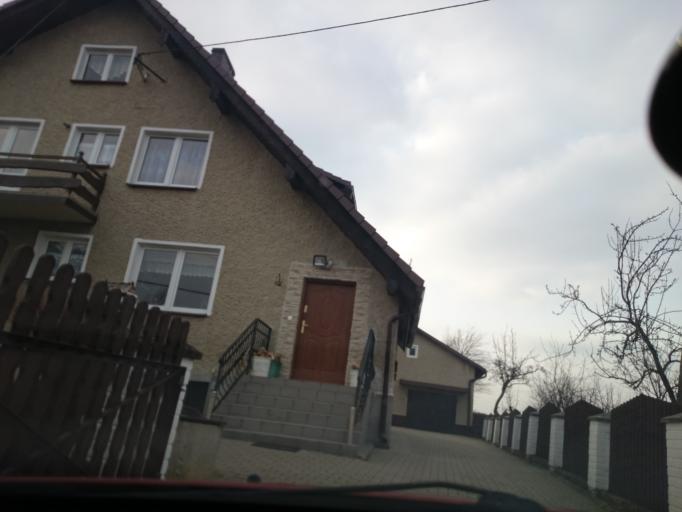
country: PL
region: Lower Silesian Voivodeship
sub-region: Powiat zabkowicki
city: Bardo
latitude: 50.5376
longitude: 16.7231
